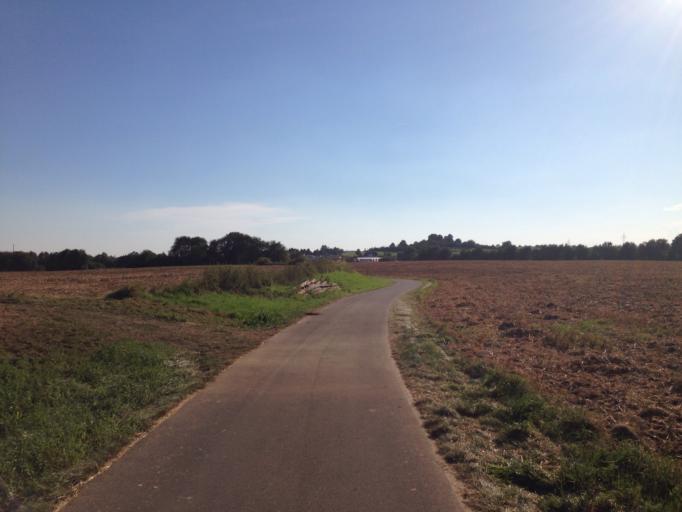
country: DE
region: Hesse
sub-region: Regierungsbezirk Giessen
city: Grunberg
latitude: 50.6088
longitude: 8.9665
